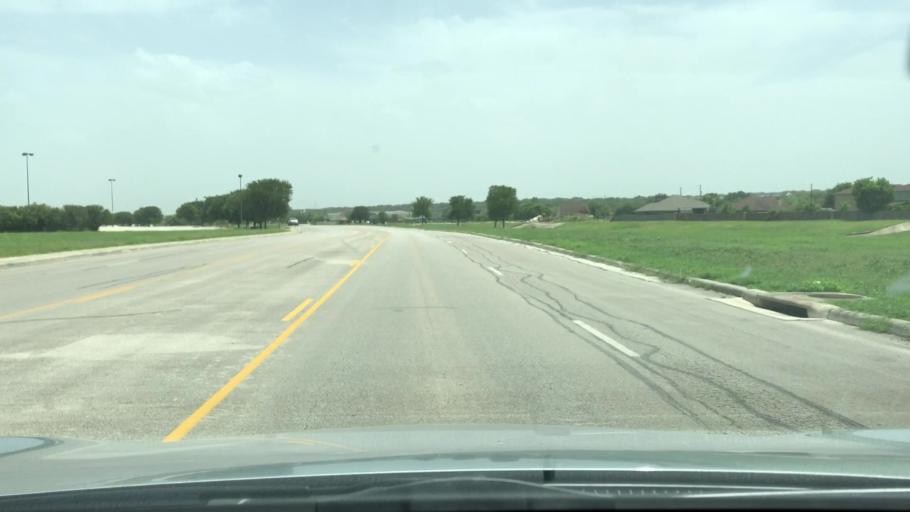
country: US
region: Texas
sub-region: Bexar County
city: Selma
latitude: 29.5861
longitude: -98.3241
